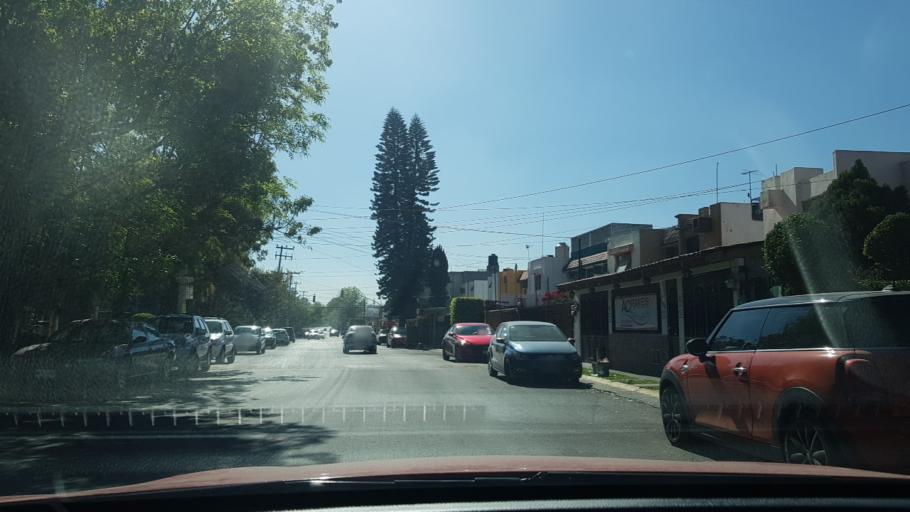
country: MX
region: Mexico
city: Cuautitlan Izcalli
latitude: 19.6510
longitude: -99.2030
